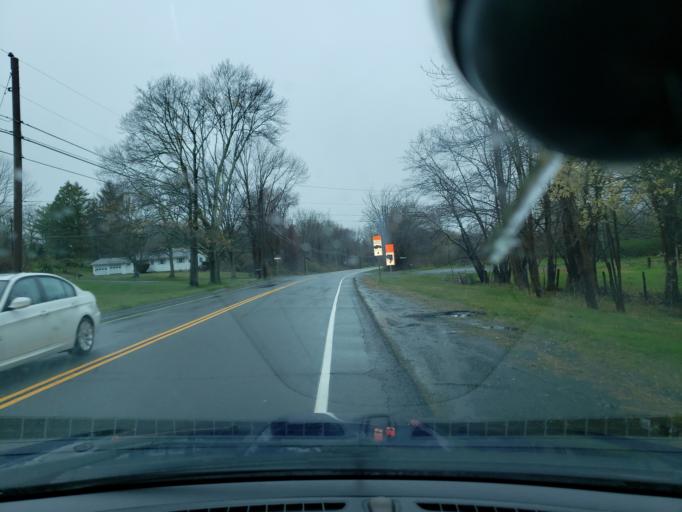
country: US
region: Connecticut
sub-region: Litchfield County
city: Bethlehem Village
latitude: 41.6746
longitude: -73.1736
